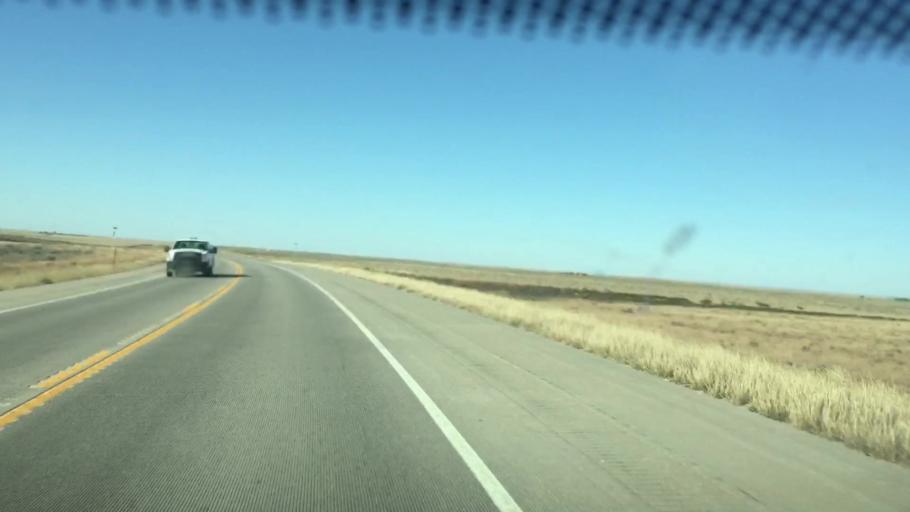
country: US
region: Colorado
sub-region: Kiowa County
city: Eads
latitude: 38.6904
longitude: -102.7757
